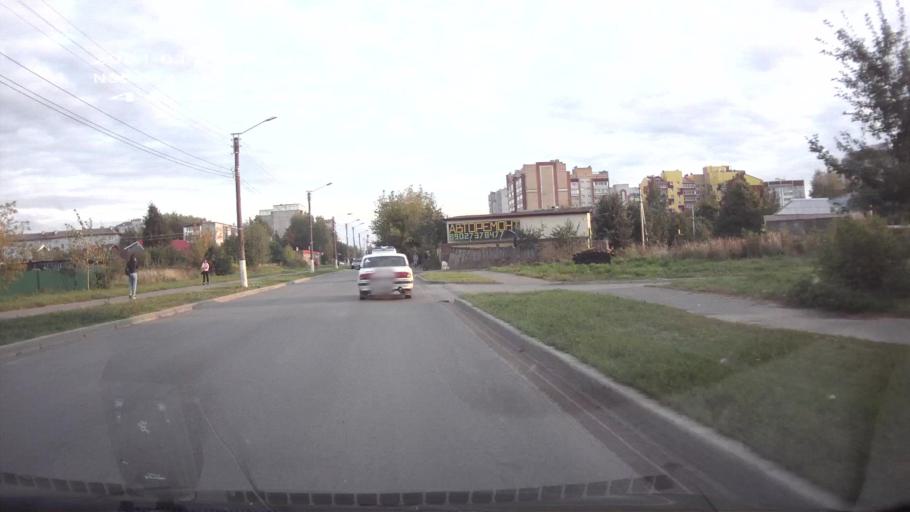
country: RU
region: Mariy-El
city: Yoshkar-Ola
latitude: 56.6480
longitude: 47.8558
